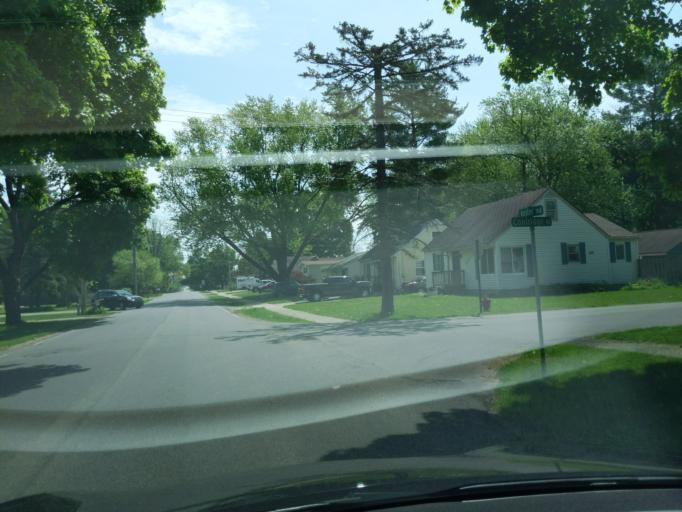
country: US
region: Michigan
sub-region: Ingham County
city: Holt
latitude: 42.6475
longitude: -84.5178
